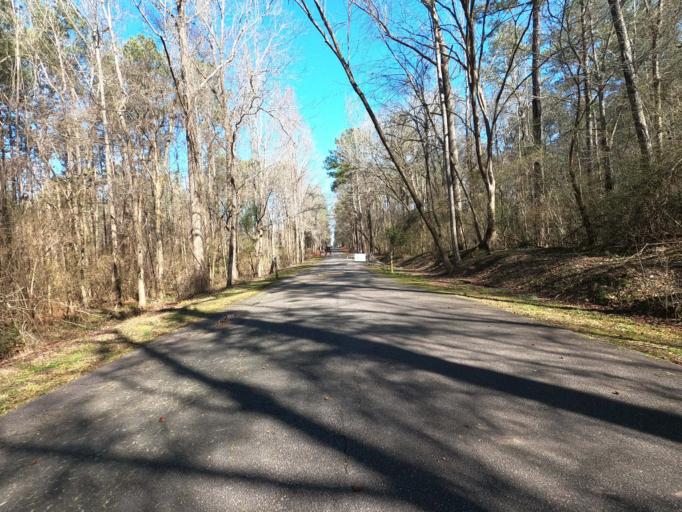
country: US
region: Georgia
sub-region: Clarke County
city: Athens
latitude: 33.9850
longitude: -83.3828
